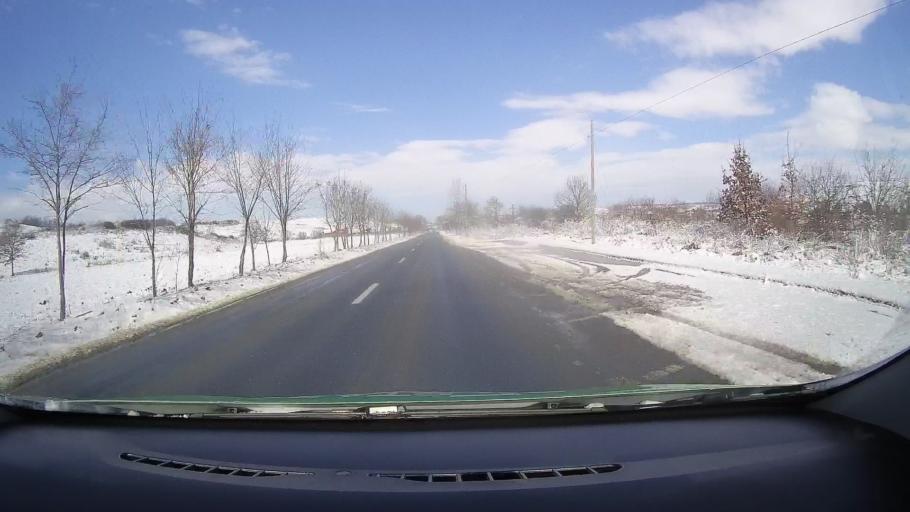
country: RO
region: Sibiu
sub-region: Comuna Nocrich
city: Nocrich
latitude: 45.8741
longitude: 24.4513
